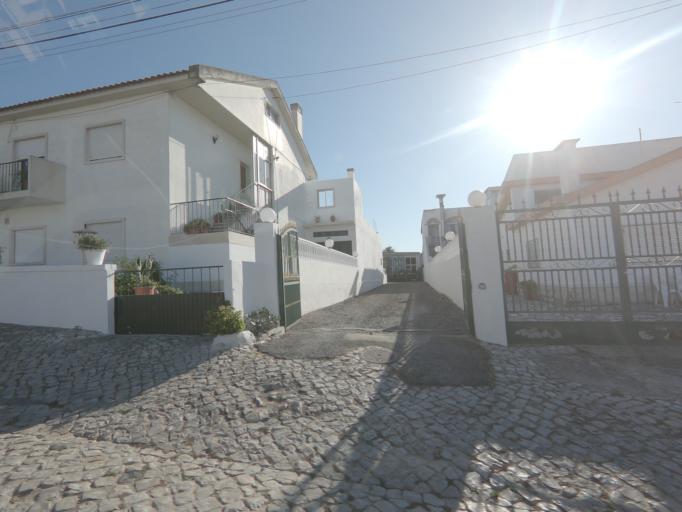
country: PT
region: Setubal
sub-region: Palmela
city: Palmela
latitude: 38.5768
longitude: -8.9074
